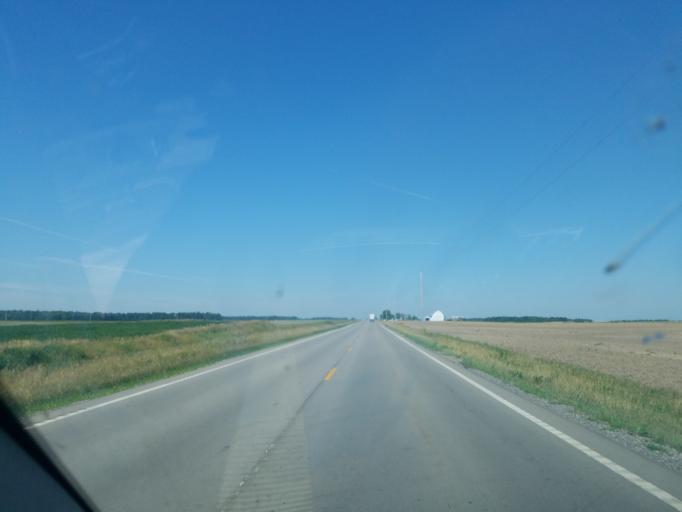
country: US
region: Ohio
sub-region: Logan County
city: Lakeview
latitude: 40.4393
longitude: -83.9683
